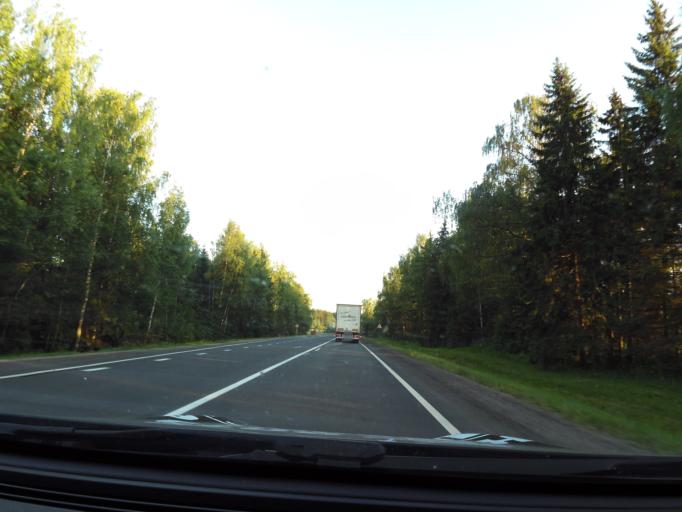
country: RU
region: Jaroslavl
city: Prechistoye
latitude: 58.4514
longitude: 40.3215
